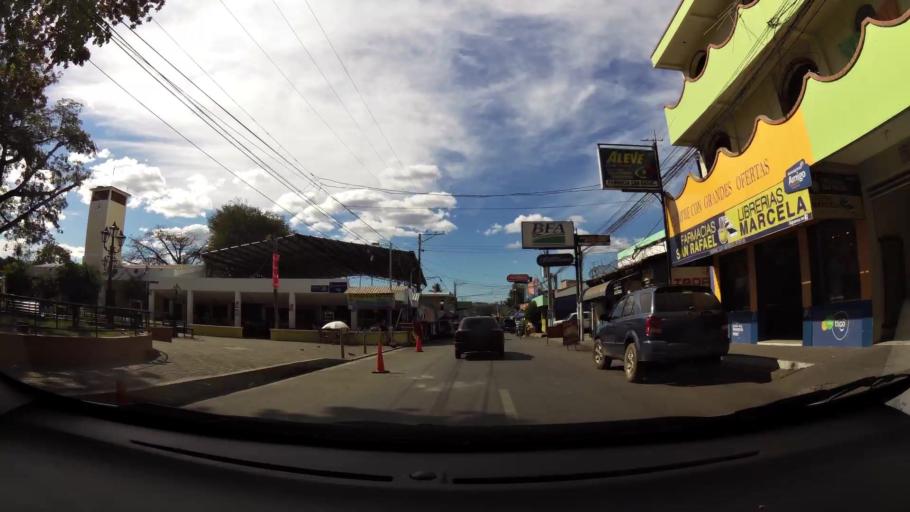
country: SV
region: San Salvador
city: Aguilares
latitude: 13.9579
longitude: -89.1872
